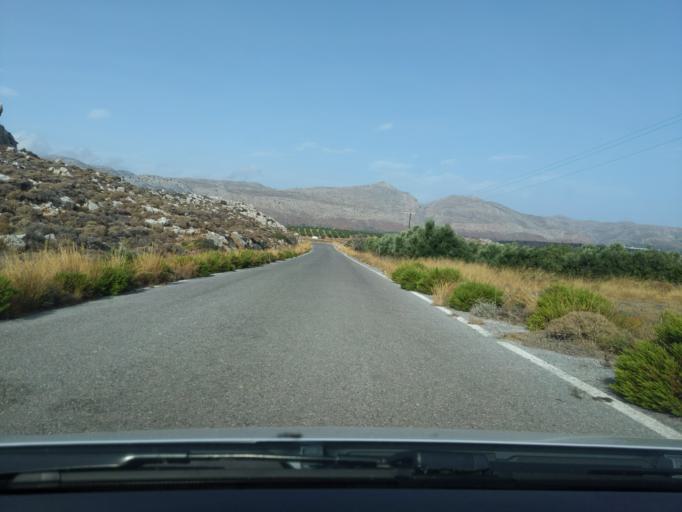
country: GR
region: Crete
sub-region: Nomos Lasithiou
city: Palekastro
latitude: 35.0859
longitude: 26.2504
